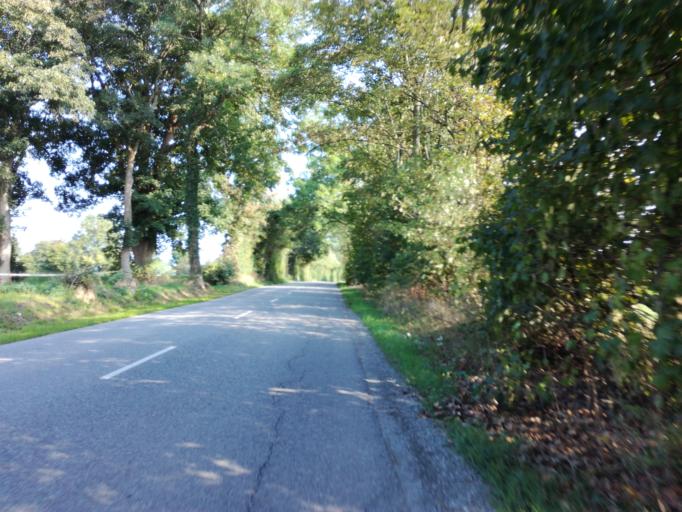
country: DK
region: South Denmark
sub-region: Vejle Kommune
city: Borkop
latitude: 55.6506
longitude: 9.6577
